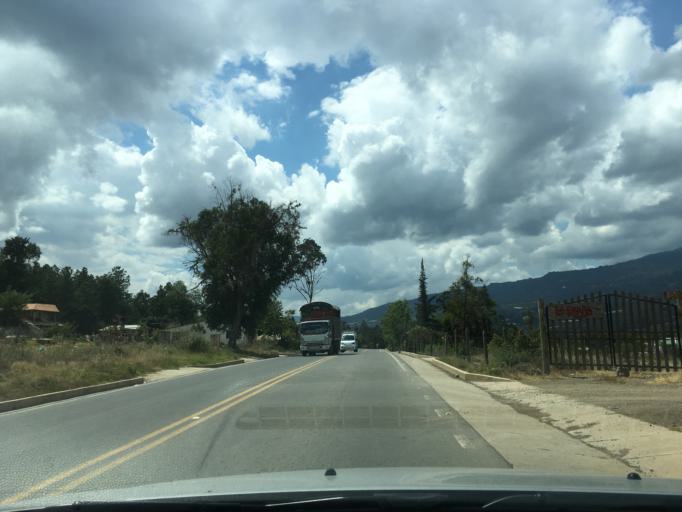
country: CO
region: Boyaca
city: Sutamarchan
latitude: 5.6215
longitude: -73.6020
